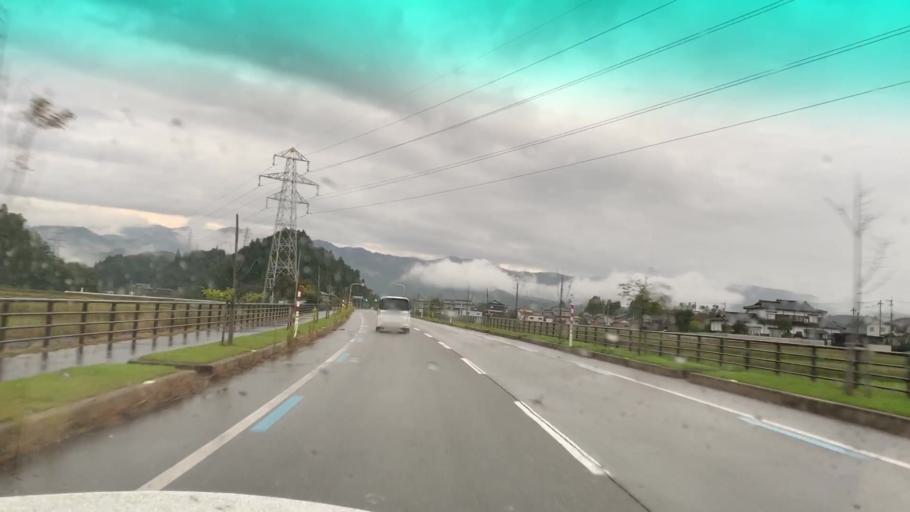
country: JP
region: Toyama
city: Kamiichi
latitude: 36.6105
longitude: 137.3245
